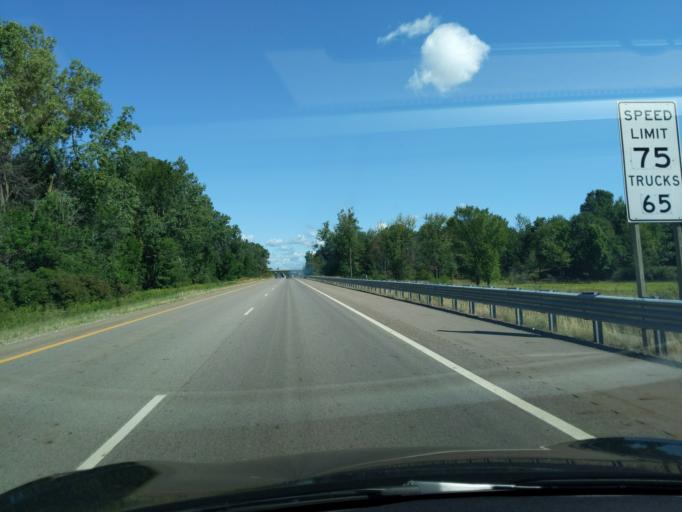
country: US
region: Michigan
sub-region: Gratiot County
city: Ithaca
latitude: 43.3303
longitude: -84.6011
